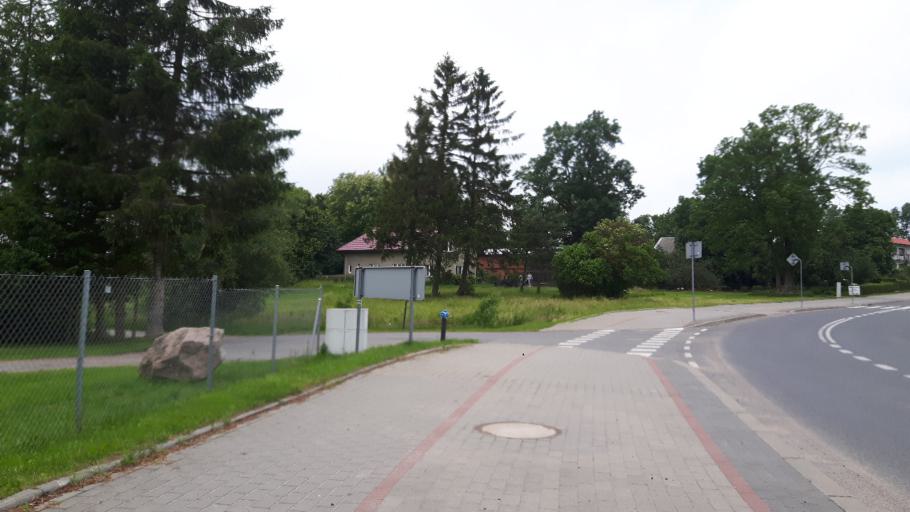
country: PL
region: West Pomeranian Voivodeship
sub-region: Powiat koszalinski
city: Sianow
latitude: 54.2940
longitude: 16.2741
